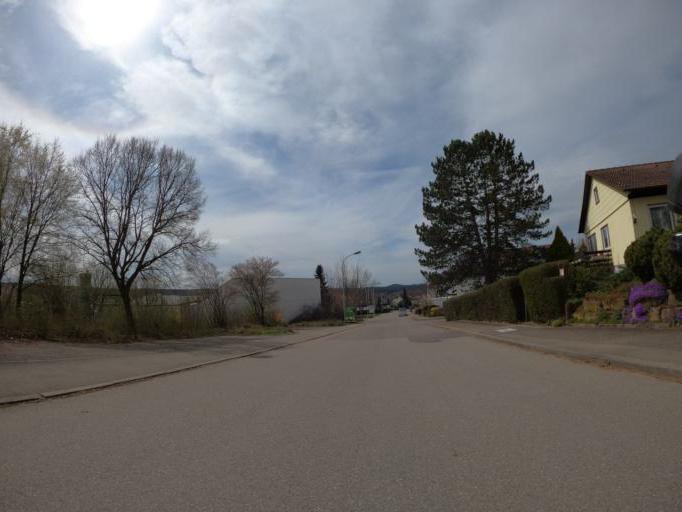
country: DE
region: Baden-Wuerttemberg
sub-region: Regierungsbezirk Stuttgart
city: Waldenbuch
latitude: 48.6424
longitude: 9.1434
